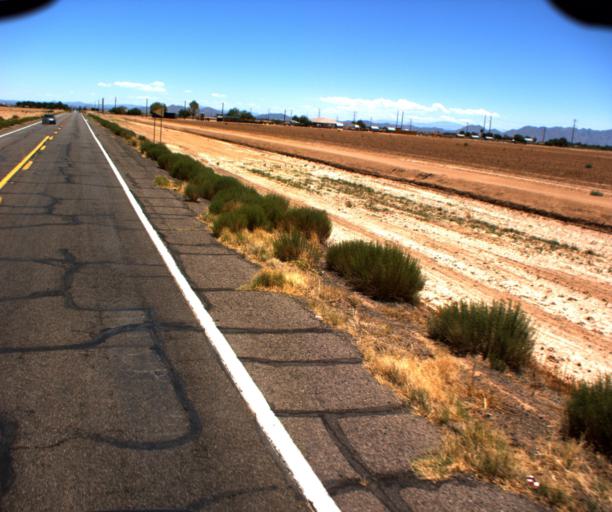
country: US
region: Arizona
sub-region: Pinal County
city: Coolidge
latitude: 32.8795
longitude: -111.5621
